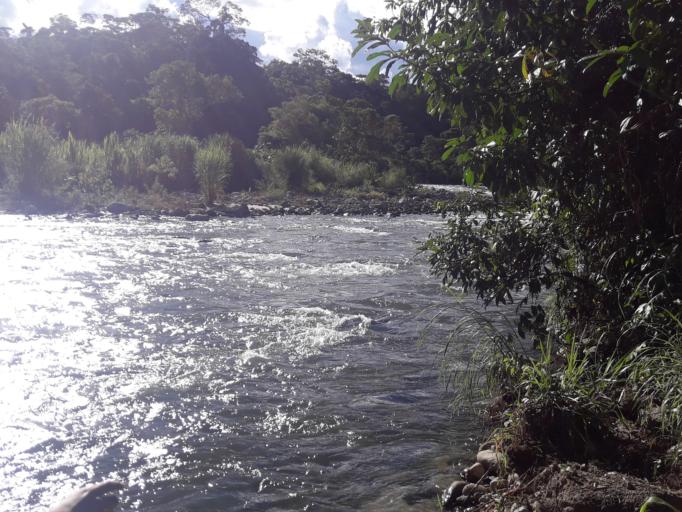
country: EC
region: Napo
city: Tena
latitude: -0.9724
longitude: -77.8569
